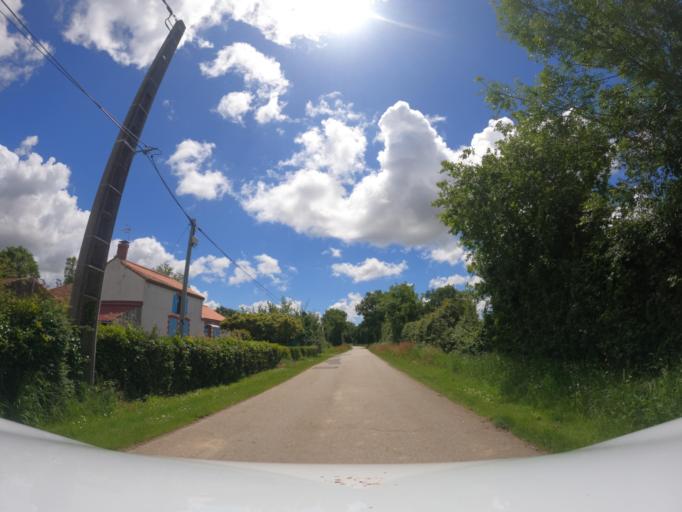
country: FR
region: Pays de la Loire
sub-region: Departement de la Vendee
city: Le Champ-Saint-Pere
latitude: 46.4902
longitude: -1.3573
